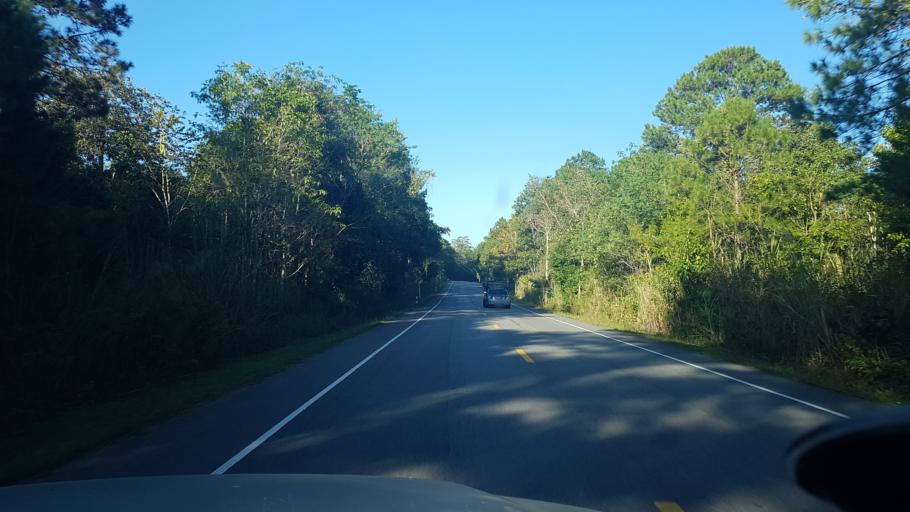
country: TH
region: Phetchabun
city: Nam Nao
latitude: 16.7258
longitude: 101.5762
